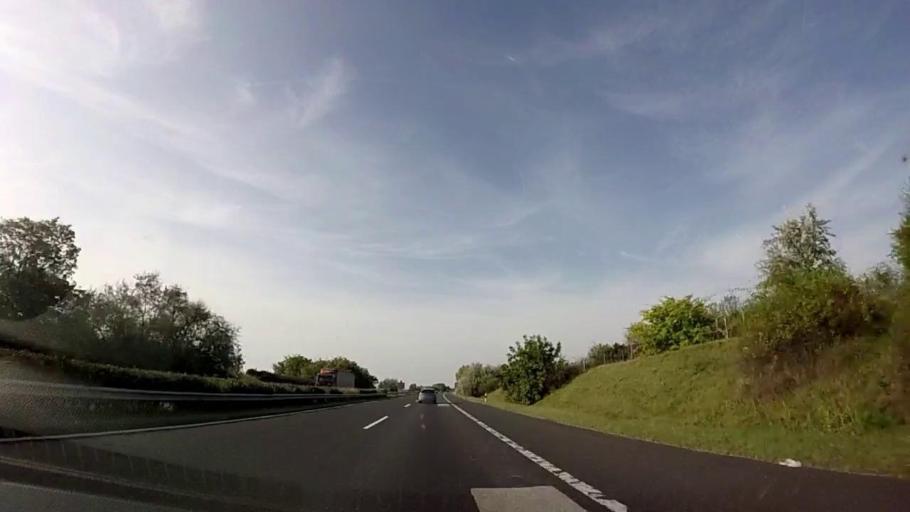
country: HU
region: Somogy
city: Balatonszabadi
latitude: 46.9260
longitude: 18.1298
